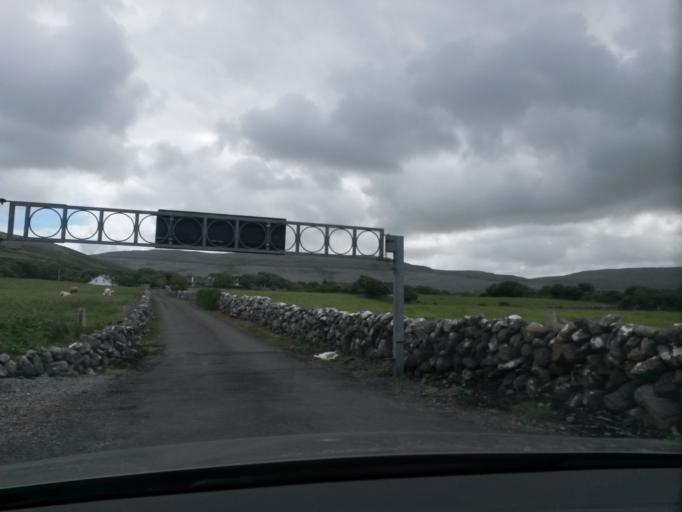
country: IE
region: Connaught
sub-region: County Galway
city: Bearna
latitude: 53.1292
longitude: -9.1281
